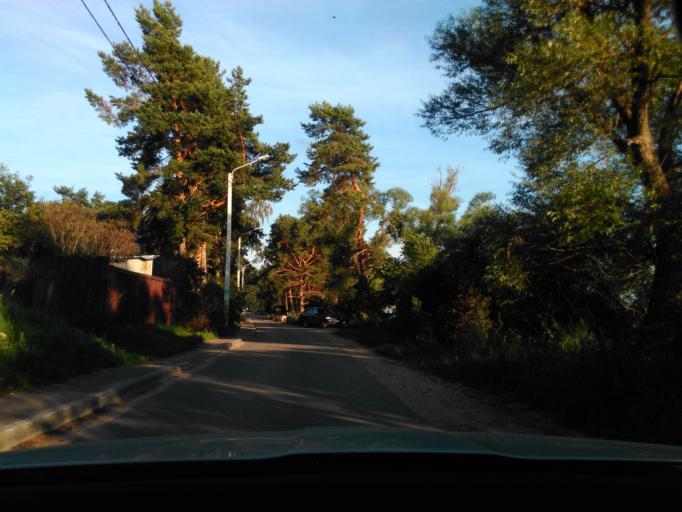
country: RU
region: Tverskaya
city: Konakovo
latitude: 56.7560
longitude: 36.7498
